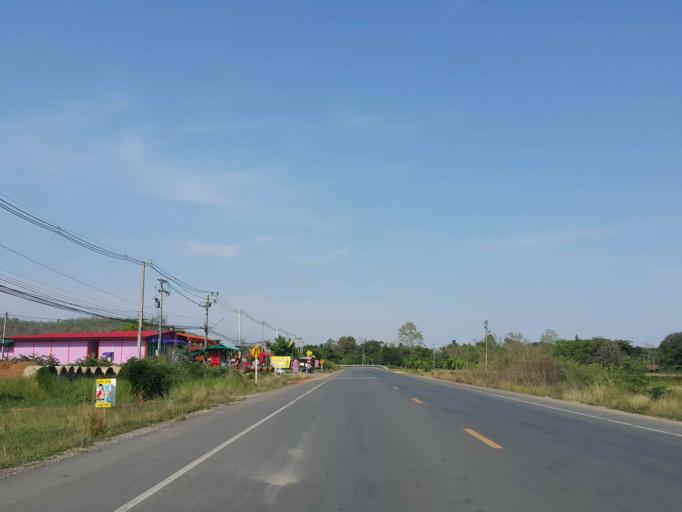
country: TH
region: Sukhothai
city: Thung Saliam
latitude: 17.3304
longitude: 99.5790
